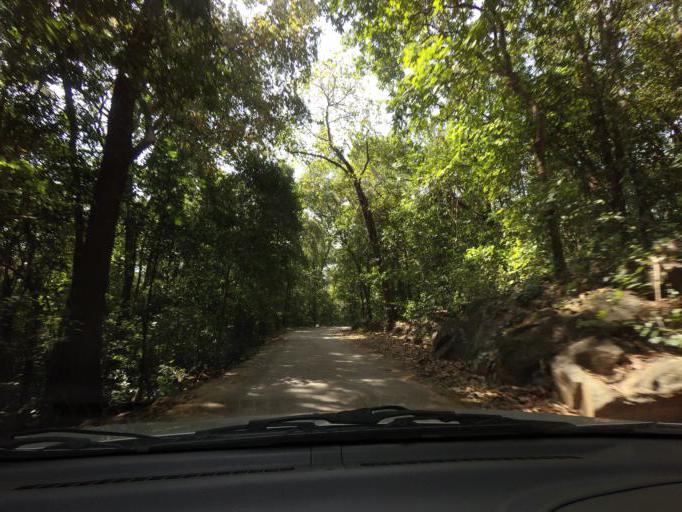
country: IN
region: Karnataka
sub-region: Kodagu
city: Somvarpet
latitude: 12.7082
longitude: 75.6476
